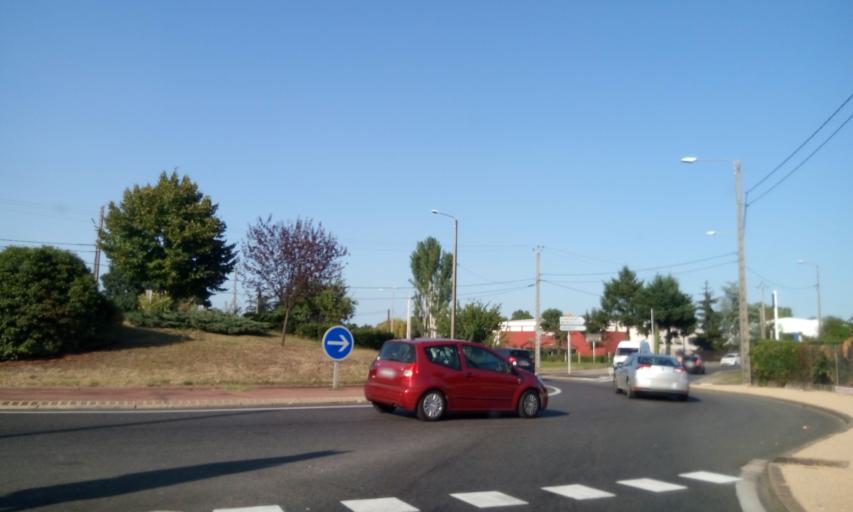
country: FR
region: Rhone-Alpes
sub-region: Departement du Rhone
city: Lissieu
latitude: 45.8708
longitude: 4.7450
